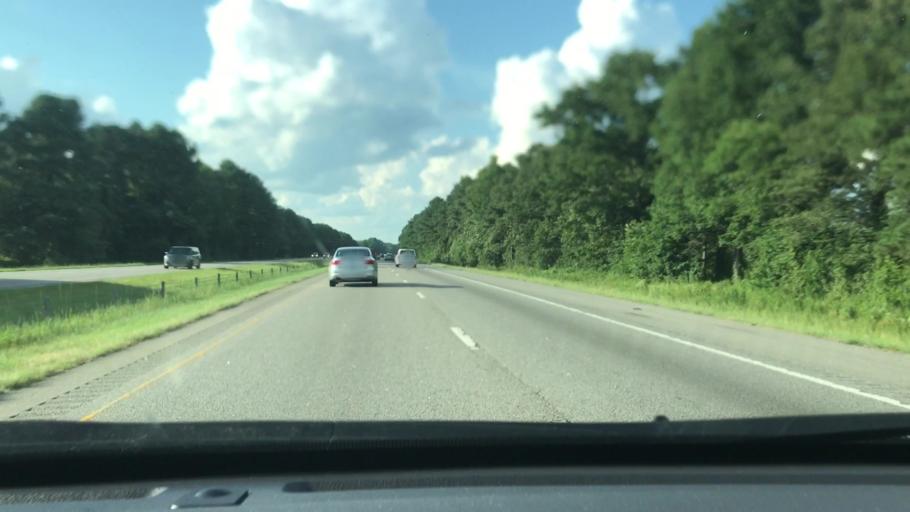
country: US
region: North Carolina
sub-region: Robeson County
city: Saint Pauls
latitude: 34.7551
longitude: -78.9970
